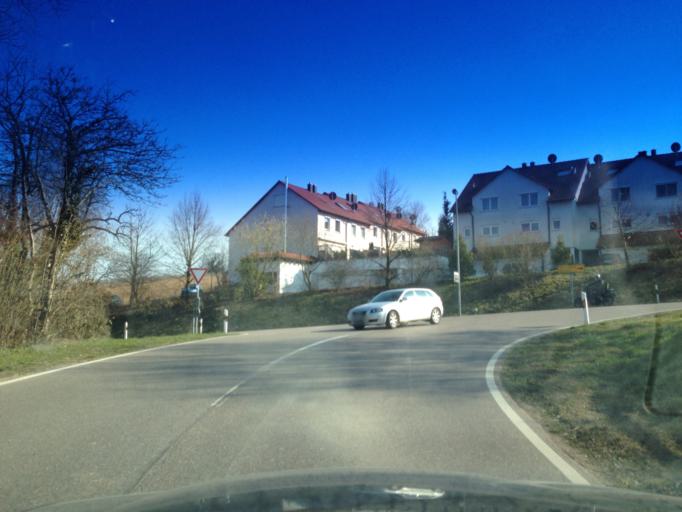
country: DE
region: Baden-Wuerttemberg
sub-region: Regierungsbezirk Stuttgart
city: Eberdingen
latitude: 48.8966
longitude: 8.9446
